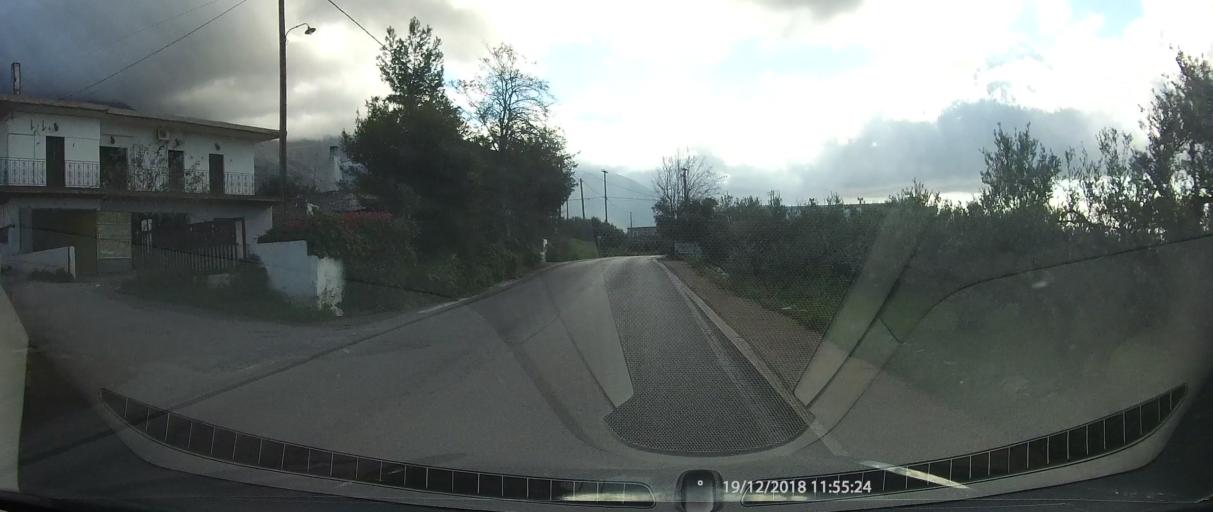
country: GR
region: Peloponnese
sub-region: Nomos Lakonias
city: Gytheio
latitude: 36.6082
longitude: 22.3940
